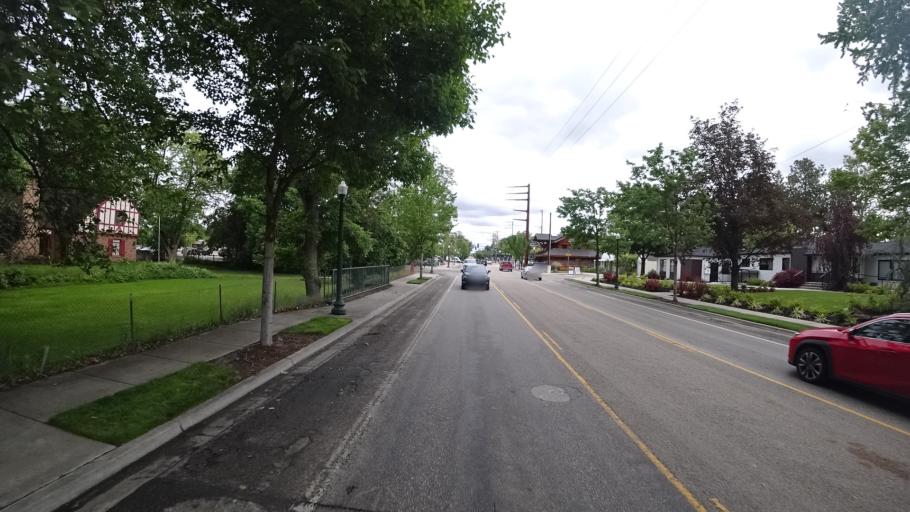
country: US
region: Idaho
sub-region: Ada County
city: Eagle
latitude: 43.6939
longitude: -116.3541
